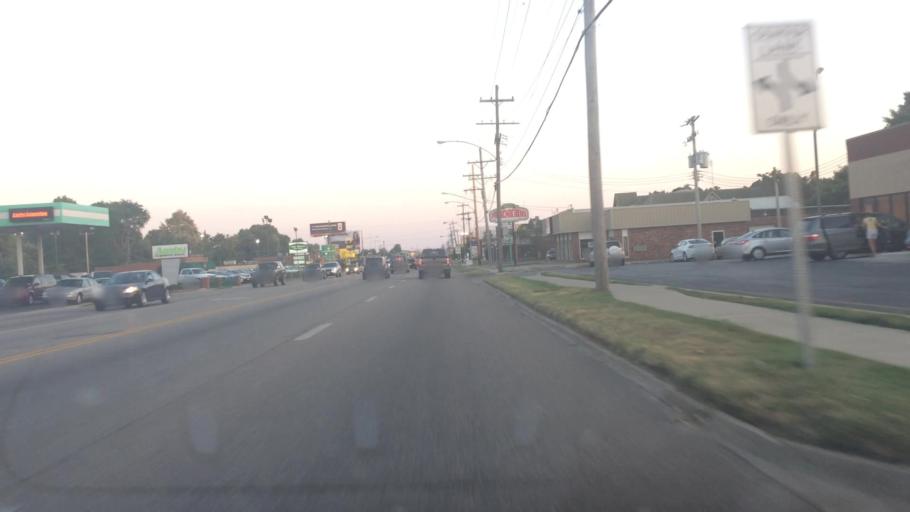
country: US
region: Missouri
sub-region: Greene County
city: Springfield
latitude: 37.1961
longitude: -93.2622
